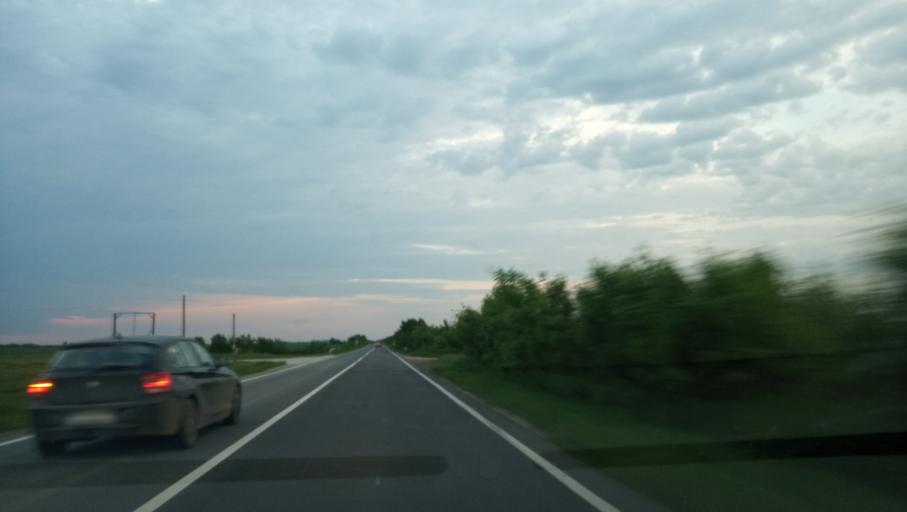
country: RO
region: Timis
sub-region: Comuna Padureni
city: Padureni
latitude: 45.5936
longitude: 21.1993
